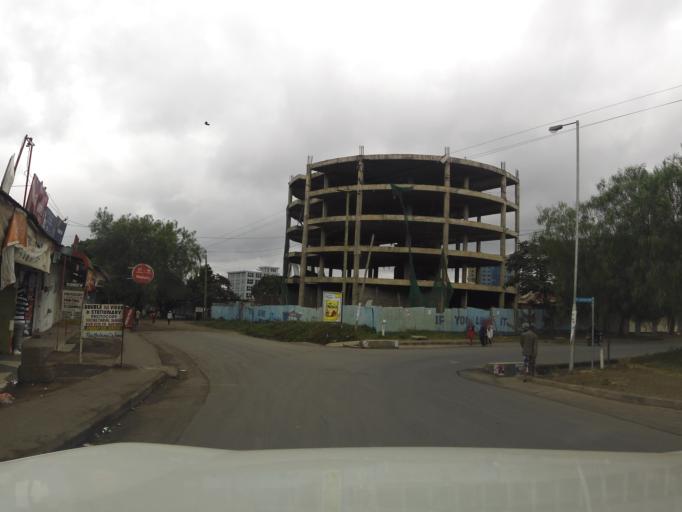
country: TZ
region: Arusha
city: Arusha
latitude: -3.3650
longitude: 36.6878
